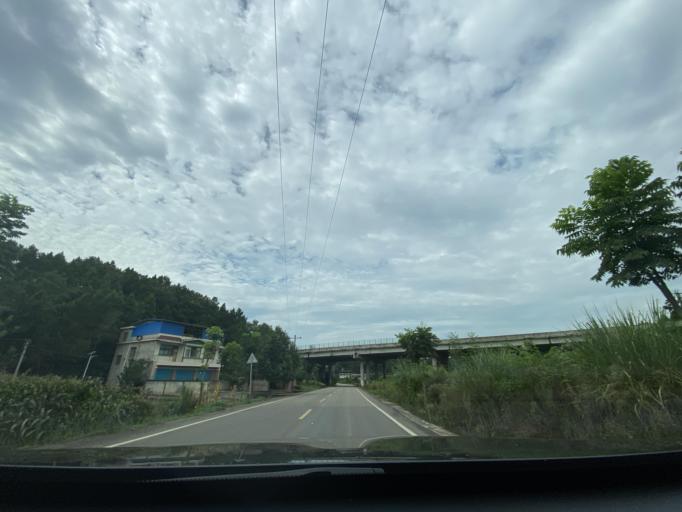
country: CN
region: Sichuan
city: Jiancheng
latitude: 30.4679
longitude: 104.6289
